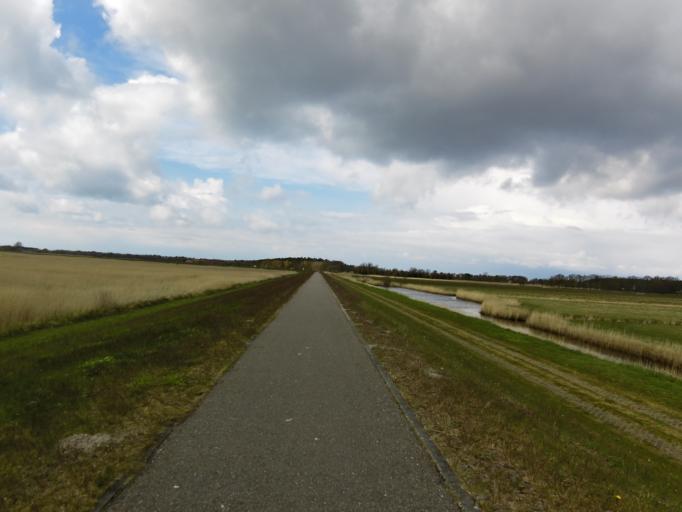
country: DE
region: Mecklenburg-Vorpommern
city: Zingst
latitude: 54.4297
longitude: 12.7273
